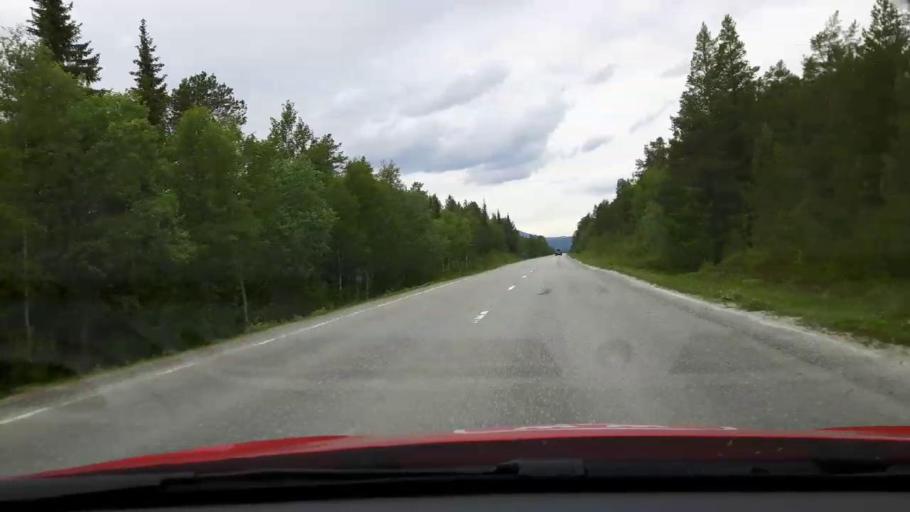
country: NO
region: Hedmark
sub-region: Engerdal
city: Engerdal
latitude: 62.5268
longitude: 12.5788
